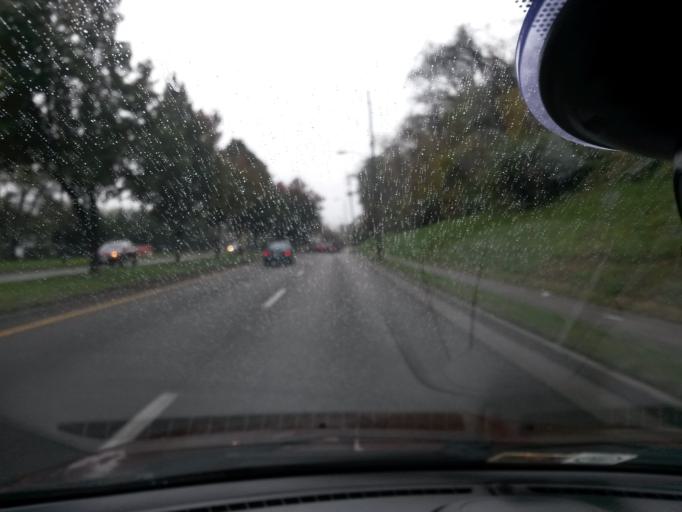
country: US
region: Virginia
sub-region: Roanoke County
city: Vinton
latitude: 37.2867
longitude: -79.9148
